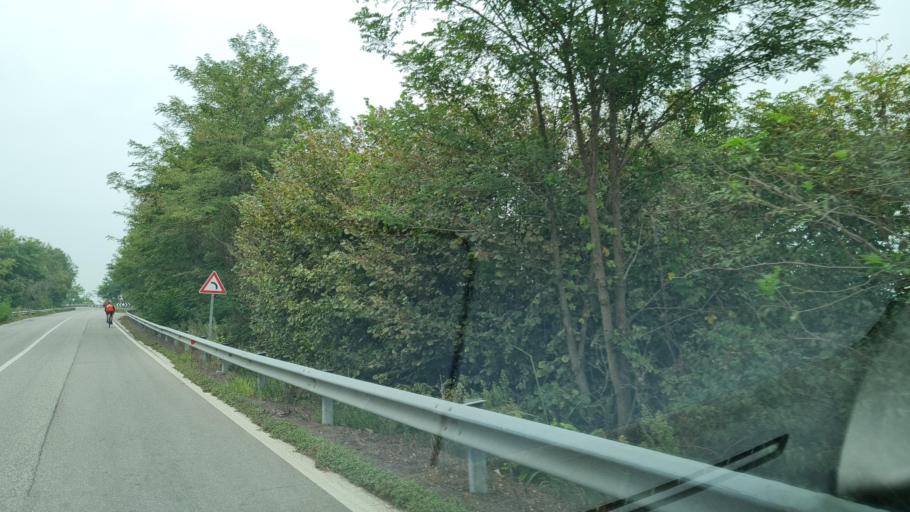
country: IT
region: Piedmont
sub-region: Provincia di Novara
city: Mandello Vitta
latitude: 45.4956
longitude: 8.4426
